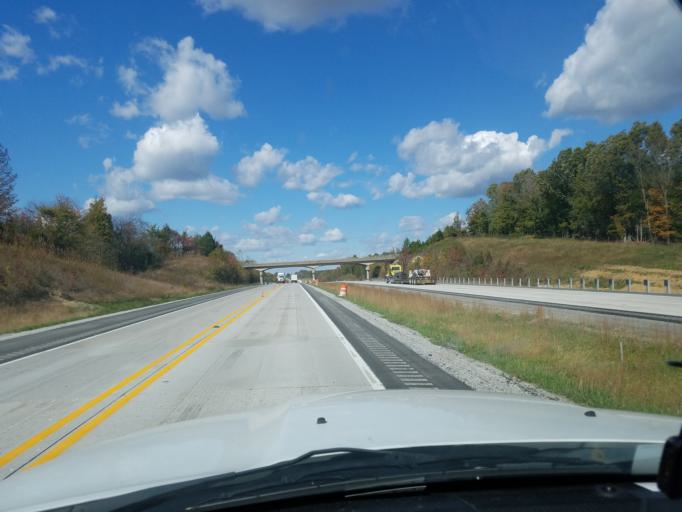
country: US
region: Kentucky
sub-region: Ohio County
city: Beaver Dam
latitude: 37.4342
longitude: -86.8505
